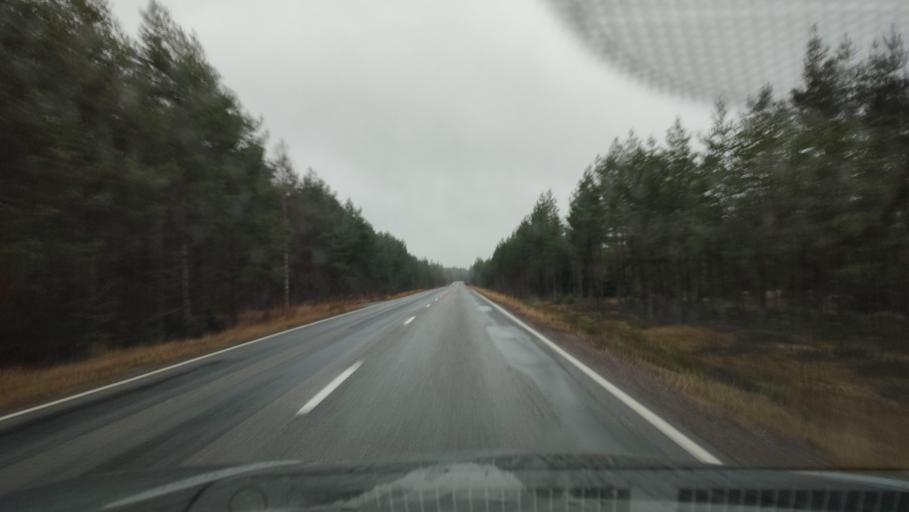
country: FI
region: Southern Ostrobothnia
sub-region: Suupohja
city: Karijoki
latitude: 62.2330
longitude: 21.7143
